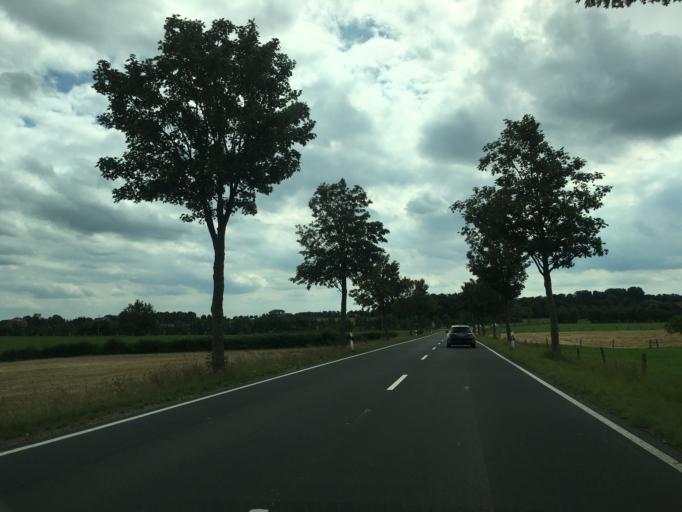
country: DE
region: North Rhine-Westphalia
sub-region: Regierungsbezirk Munster
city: Nordkirchen
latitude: 51.7743
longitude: 7.5454
